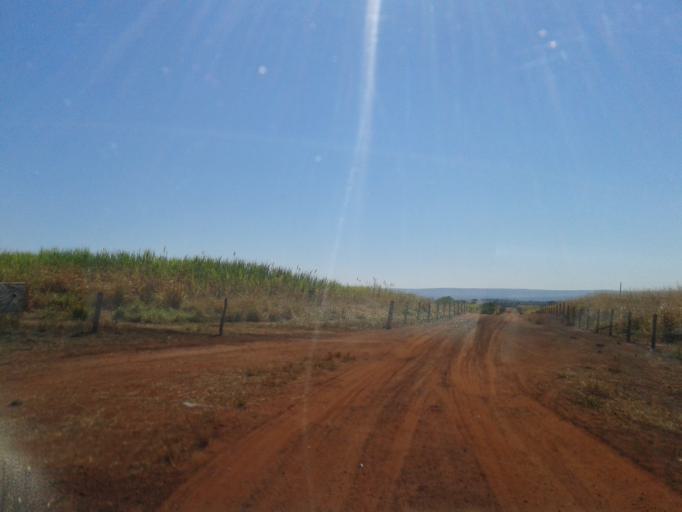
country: BR
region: Minas Gerais
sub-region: Santa Vitoria
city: Santa Vitoria
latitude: -19.1497
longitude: -50.2041
